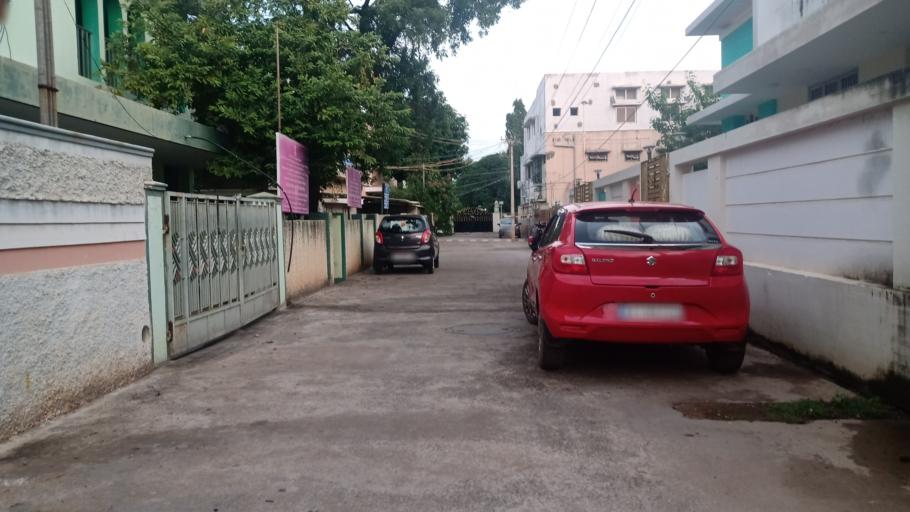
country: IN
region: Tamil Nadu
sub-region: Tiruchchirappalli
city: Tiruchirappalli
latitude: 10.7819
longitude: 78.6907
